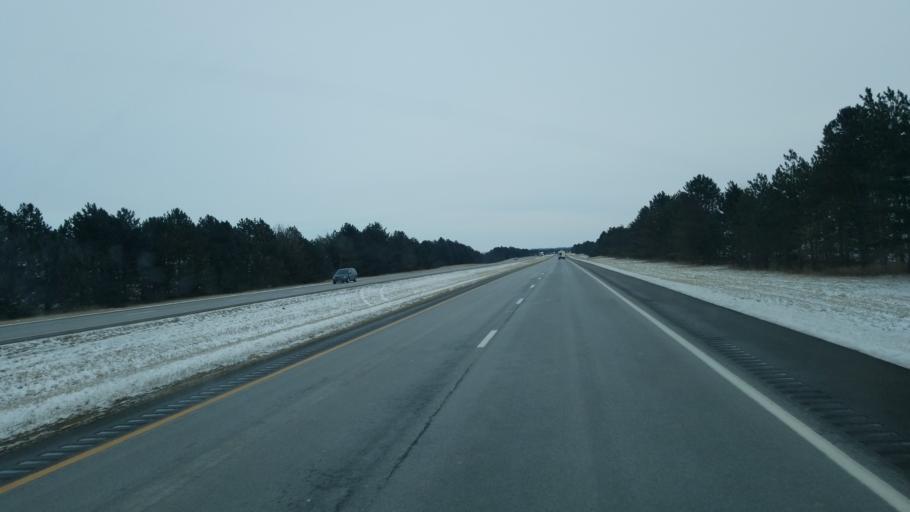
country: US
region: Ohio
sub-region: Wyandot County
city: Carey
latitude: 40.9545
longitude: -83.4387
